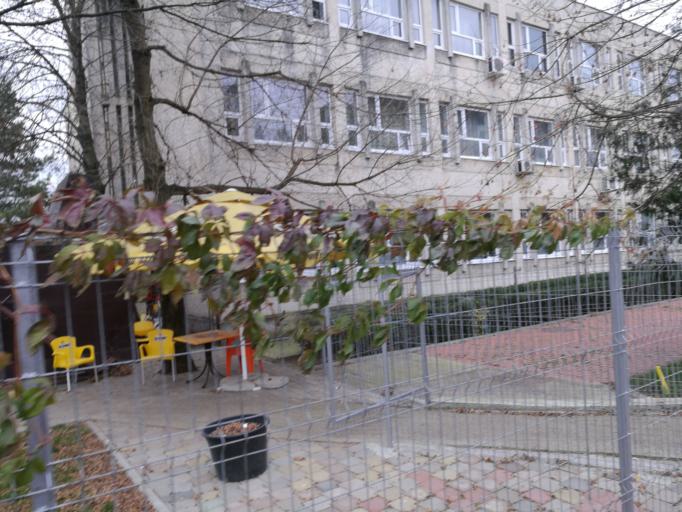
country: RO
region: Suceava
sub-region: Comuna Scheia
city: Scheia
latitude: 47.6705
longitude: 26.2681
